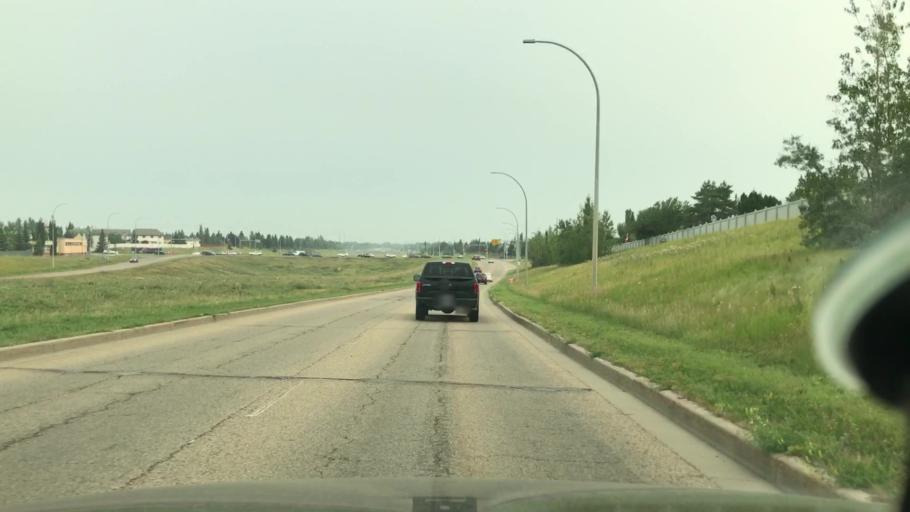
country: CA
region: Alberta
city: Edmonton
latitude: 53.4655
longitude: -113.5837
